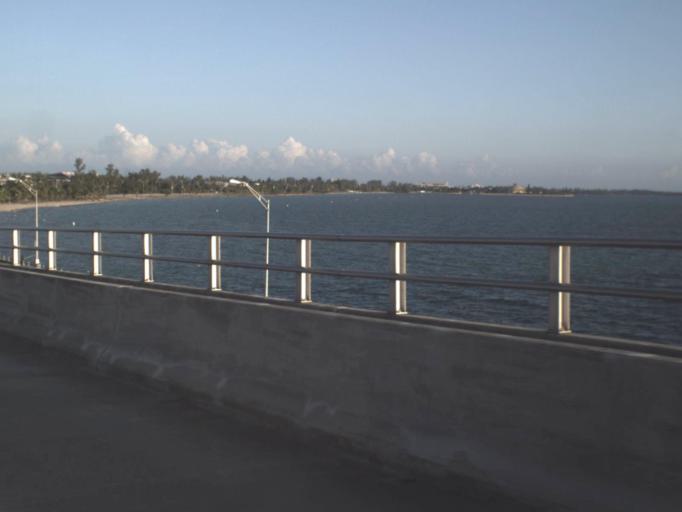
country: US
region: Florida
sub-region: Miami-Dade County
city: Miami
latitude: 25.7465
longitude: -80.1809
